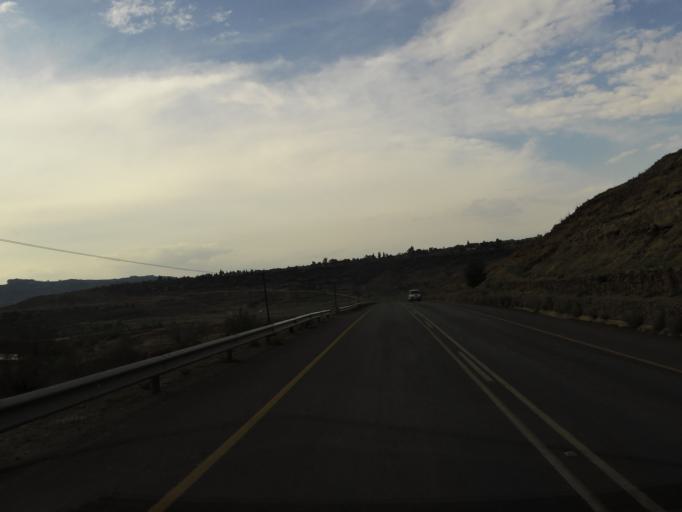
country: LS
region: Maseru
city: Maseru
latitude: -29.3850
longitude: 27.5032
